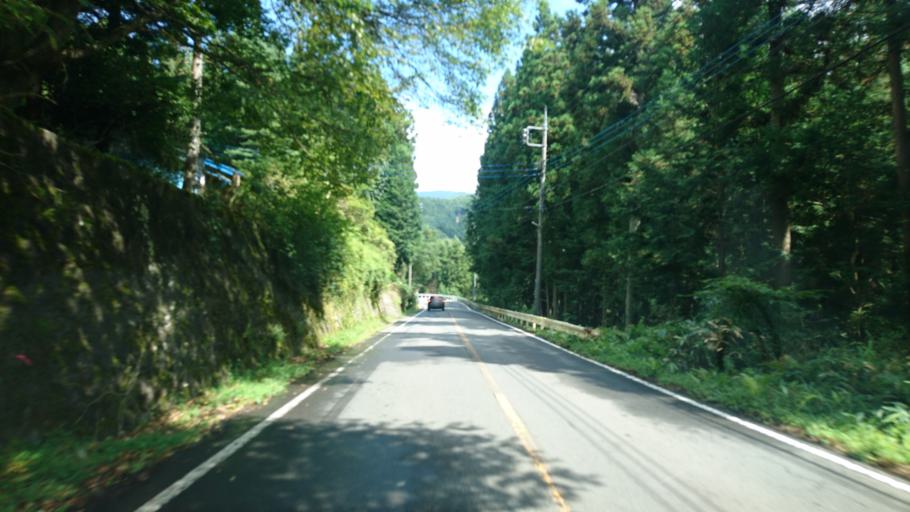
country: JP
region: Gunma
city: Omamacho-omama
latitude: 36.6053
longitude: 139.2336
